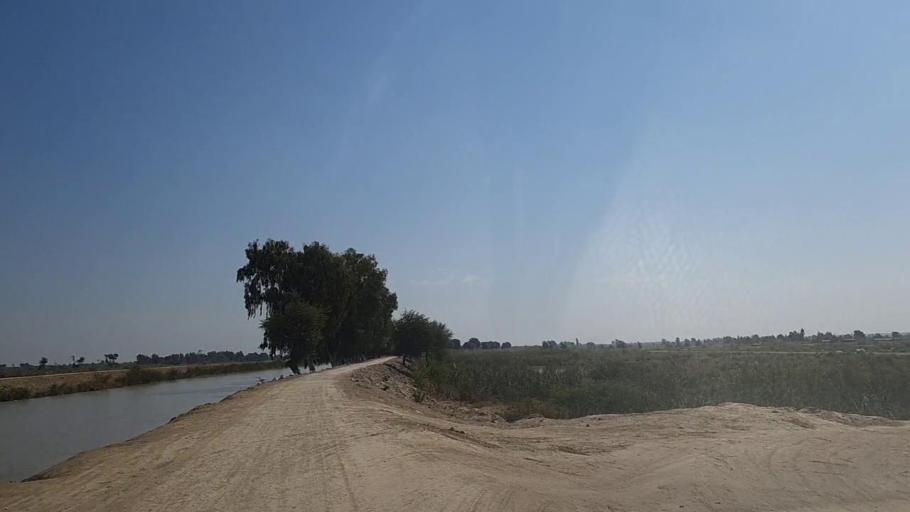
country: PK
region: Sindh
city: Samaro
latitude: 25.3766
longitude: 69.3303
